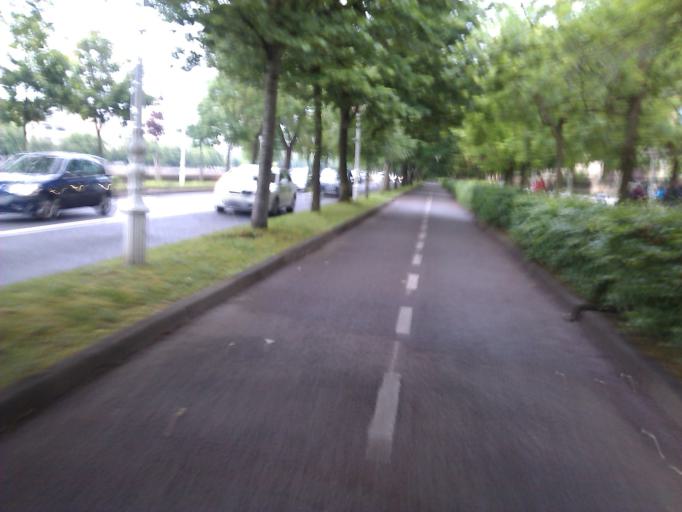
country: ES
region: Basque Country
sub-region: Provincia de Guipuzcoa
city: San Sebastian
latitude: 43.3155
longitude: -1.9793
